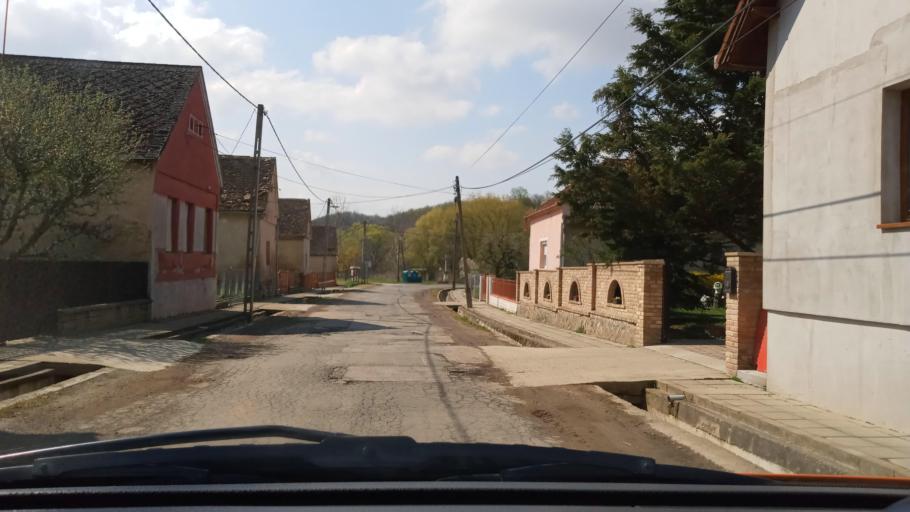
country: HU
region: Baranya
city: Boly
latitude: 46.0758
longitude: 18.5134
